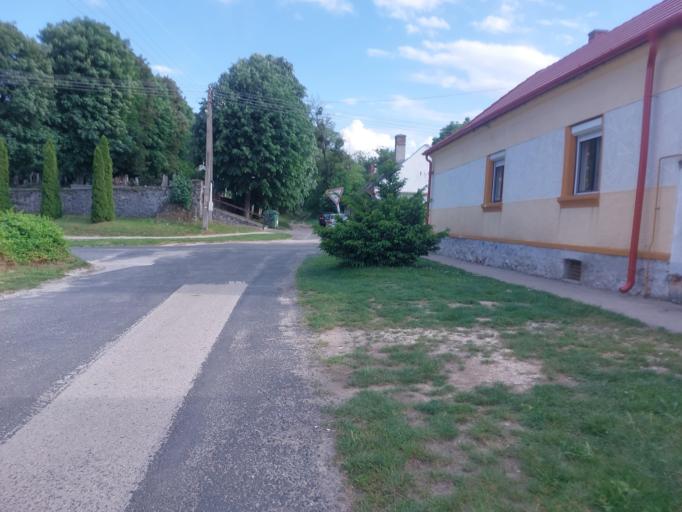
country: HU
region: Veszprem
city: Devecser
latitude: 47.1657
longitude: 17.3815
